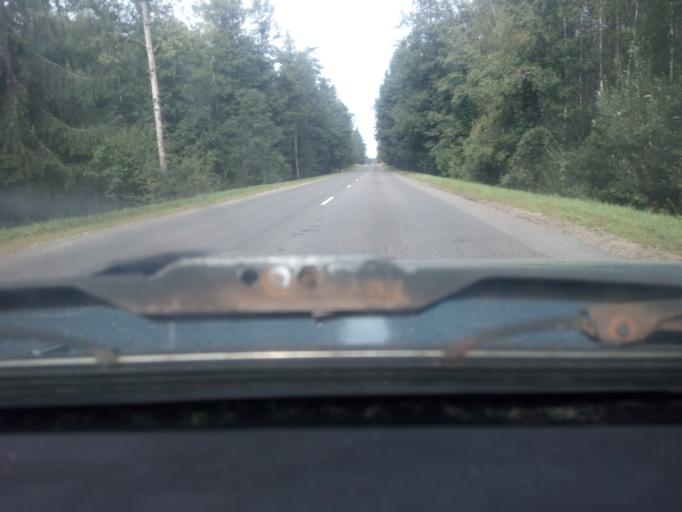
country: BY
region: Vitebsk
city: Vyerkhnyadzvinsk
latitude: 55.7956
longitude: 27.9609
